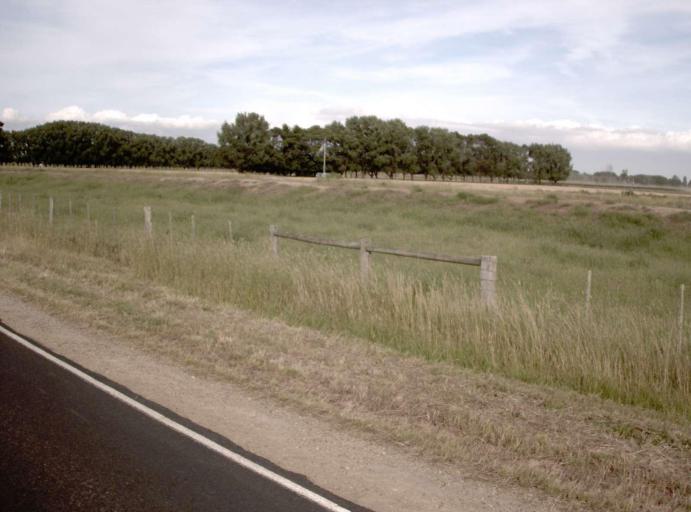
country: AU
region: Victoria
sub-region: Wellington
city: Heyfield
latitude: -38.0139
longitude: 146.7741
